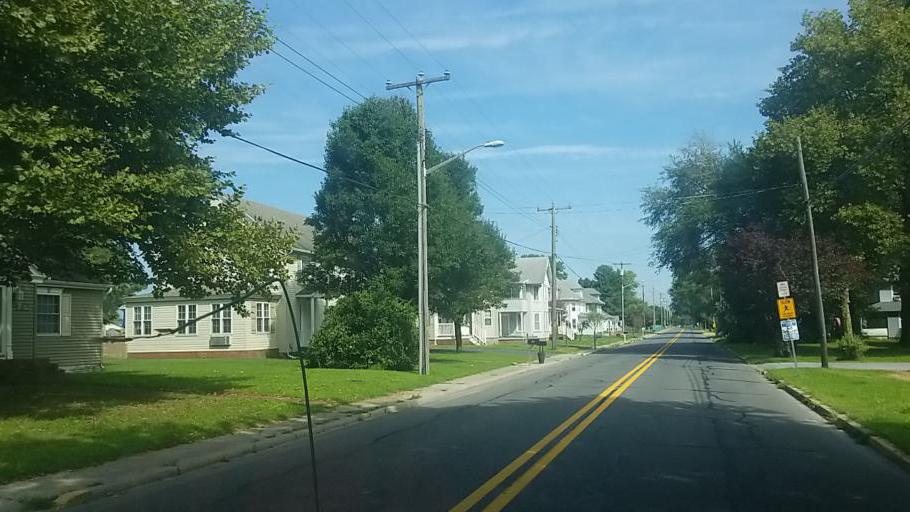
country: US
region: Delaware
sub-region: Sussex County
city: Selbyville
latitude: 38.5195
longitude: -75.2362
